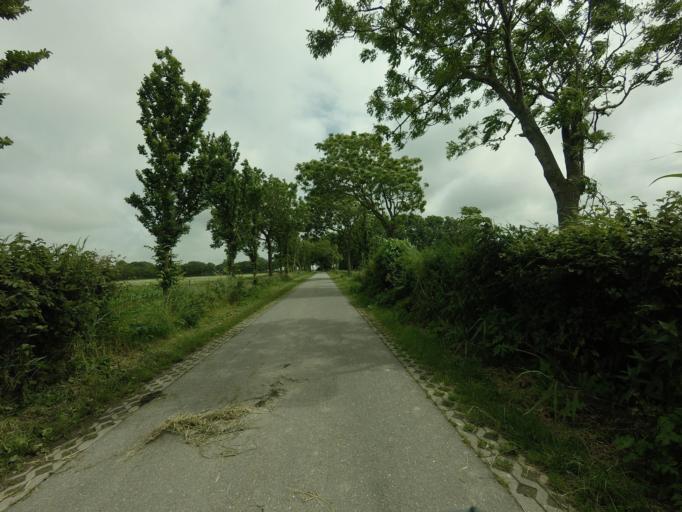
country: NL
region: North Holland
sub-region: Gemeente Schagen
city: Harenkarspel
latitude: 52.7344
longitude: 4.7219
